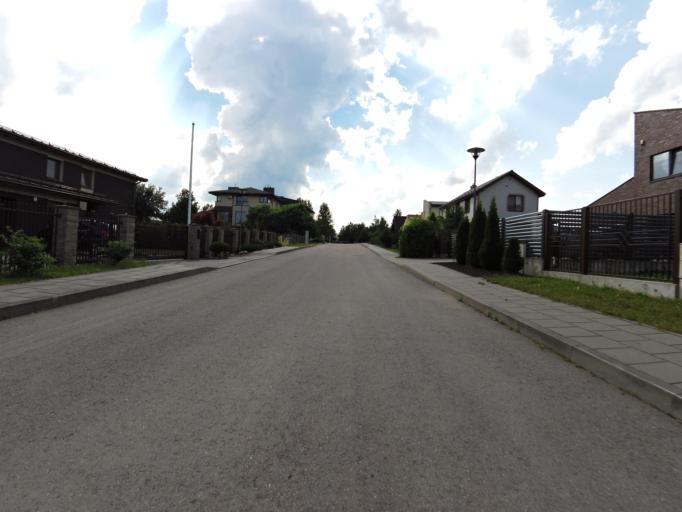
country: LT
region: Vilnius County
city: Pasilaiciai
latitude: 54.7632
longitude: 25.2289
